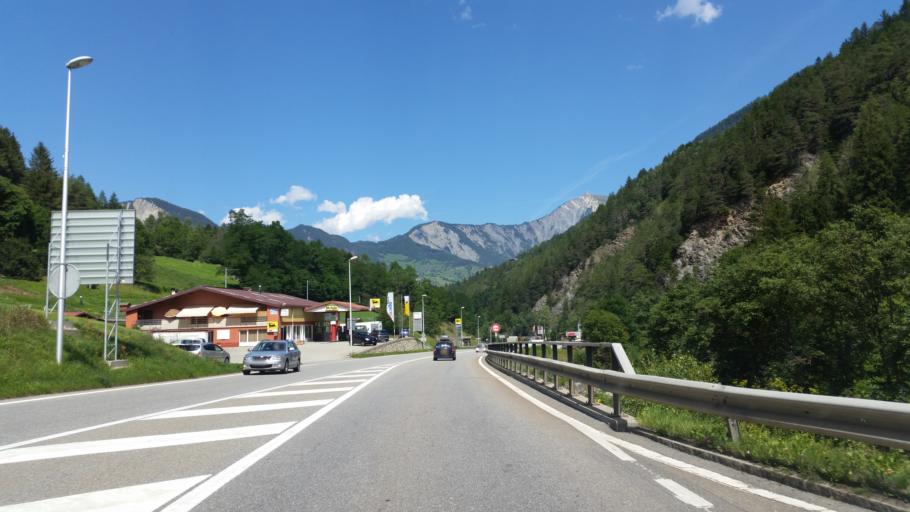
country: CH
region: Valais
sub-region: Entremont District
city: Orsieres
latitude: 46.0404
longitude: 7.1472
